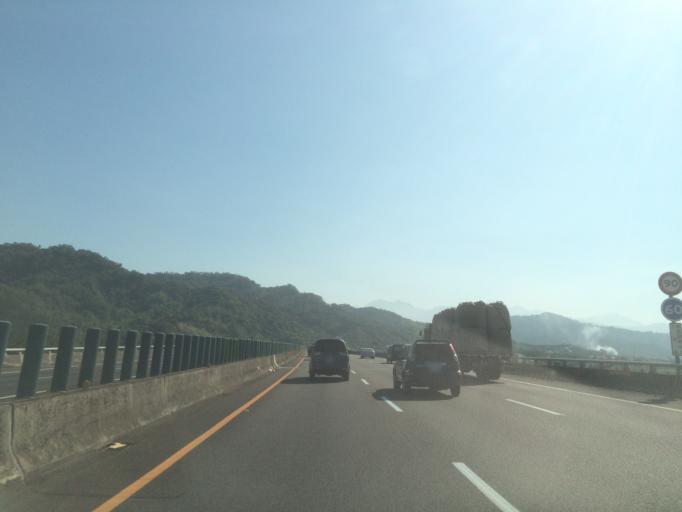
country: TW
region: Taiwan
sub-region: Nantou
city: Nantou
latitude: 23.9121
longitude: 120.6960
